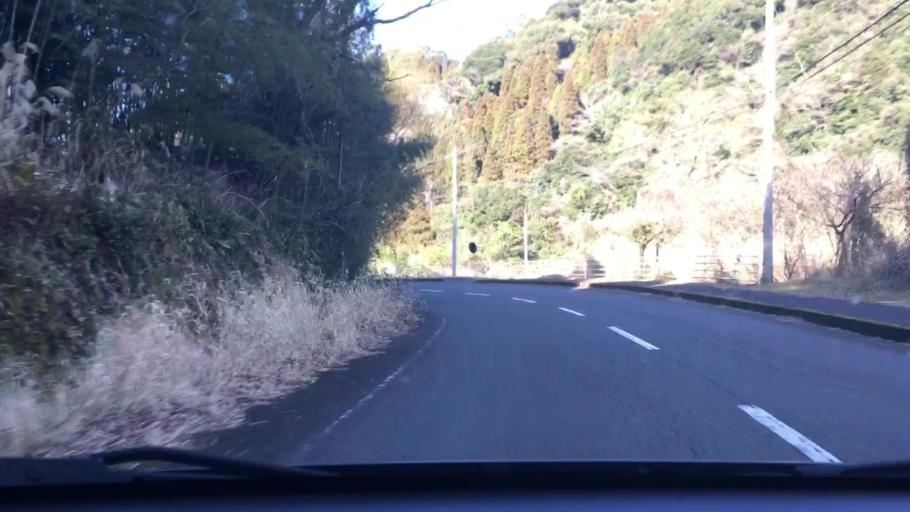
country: JP
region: Kagoshima
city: Satsumasendai
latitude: 31.7546
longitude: 130.4105
